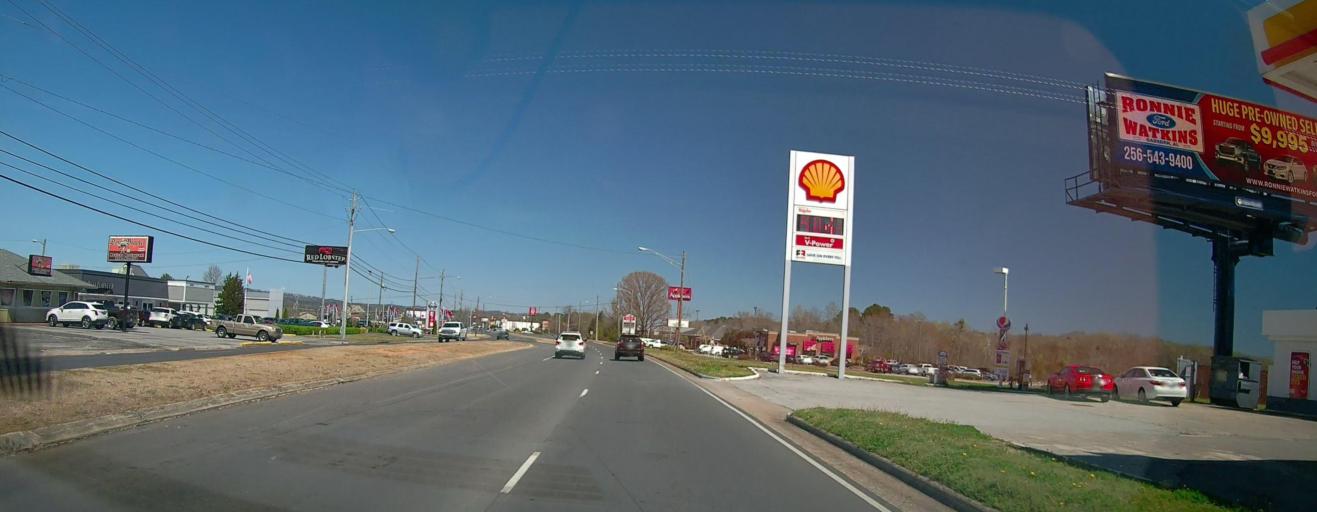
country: US
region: Alabama
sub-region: Etowah County
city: Gadsden
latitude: 33.9798
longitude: -86.0075
